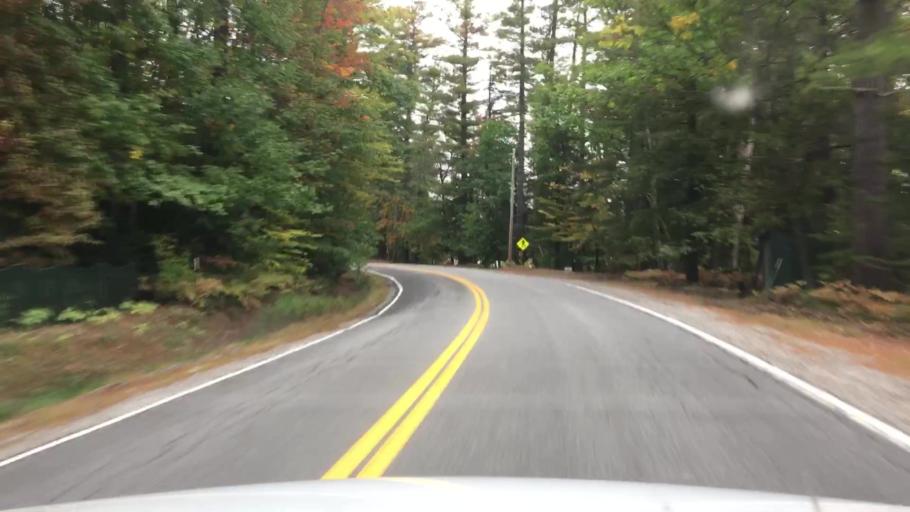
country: US
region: Maine
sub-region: Oxford County
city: Bethel
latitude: 44.3620
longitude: -70.7953
